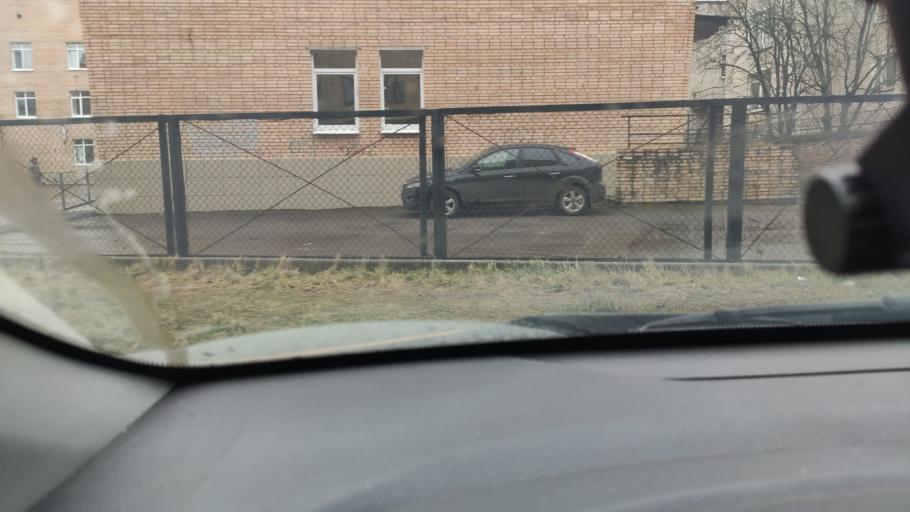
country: RU
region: Moskovskaya
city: Selyatino
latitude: 55.5111
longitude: 36.9746
